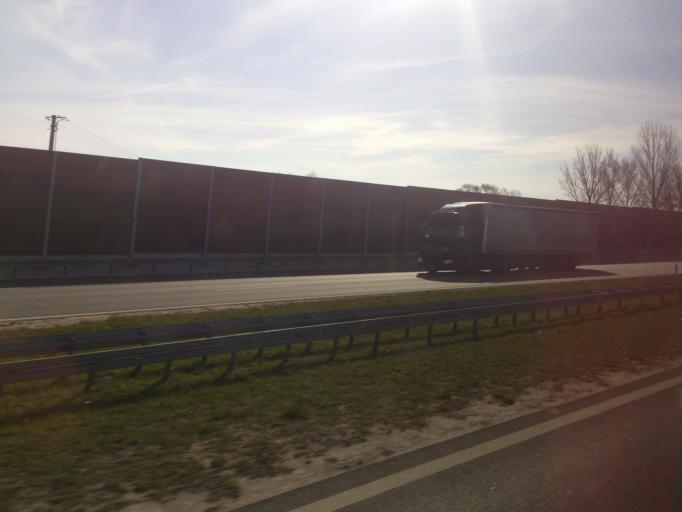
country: PL
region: Kujawsko-Pomorskie
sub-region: Powiat aleksandrowski
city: Raciazek
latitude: 52.8085
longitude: 18.8151
